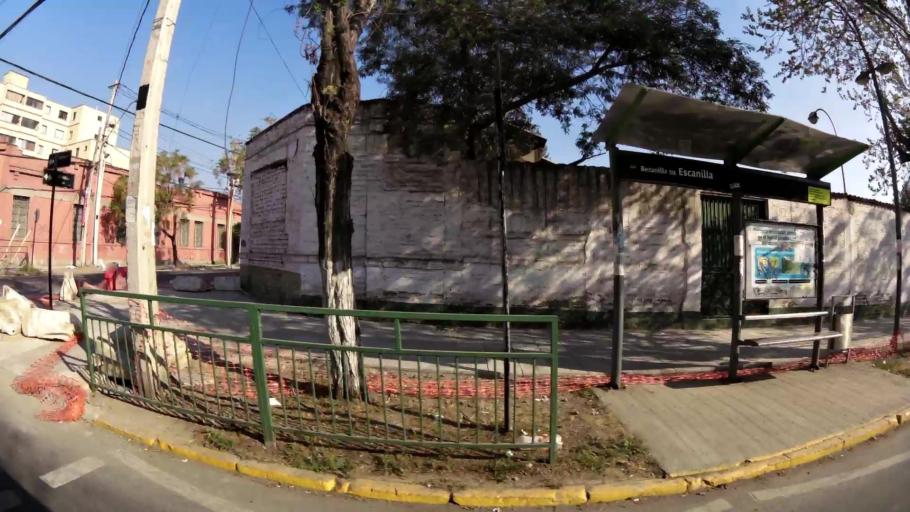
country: CL
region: Santiago Metropolitan
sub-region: Provincia de Santiago
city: Santiago
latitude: -33.4178
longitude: -70.6608
